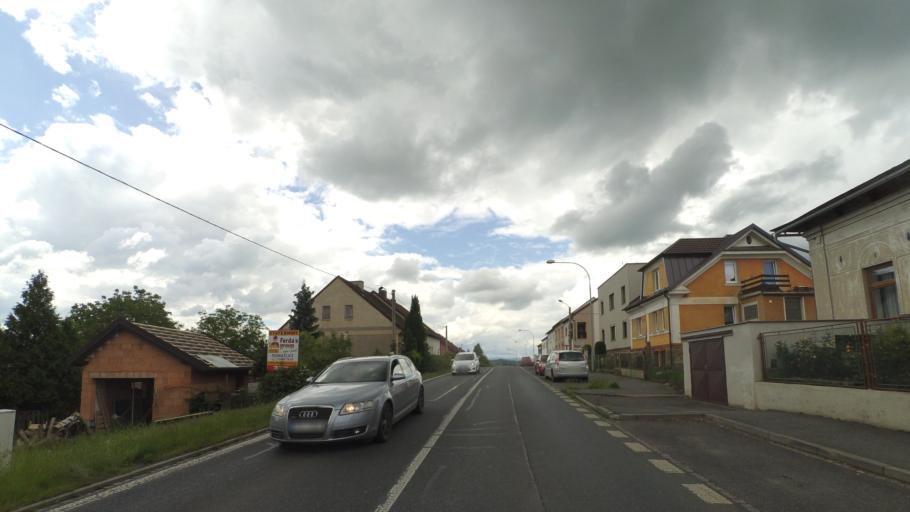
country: CZ
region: Plzensky
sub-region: Okres Domazlice
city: Kdyne
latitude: 49.3908
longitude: 13.0350
